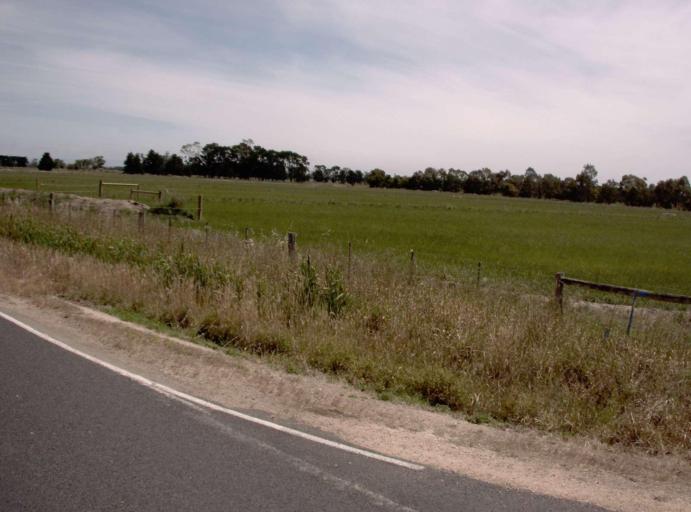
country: AU
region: Victoria
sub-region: Wellington
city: Heyfield
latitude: -38.0355
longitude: 146.8782
